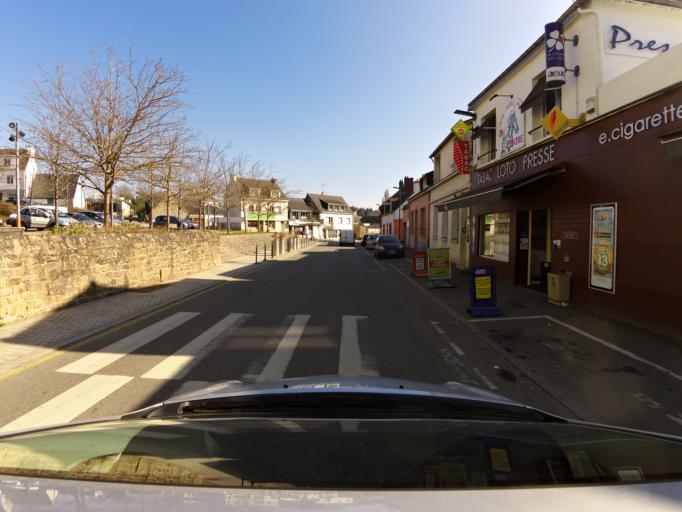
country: FR
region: Brittany
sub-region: Departement du Morbihan
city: Hennebont
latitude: 47.8262
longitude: -3.2510
